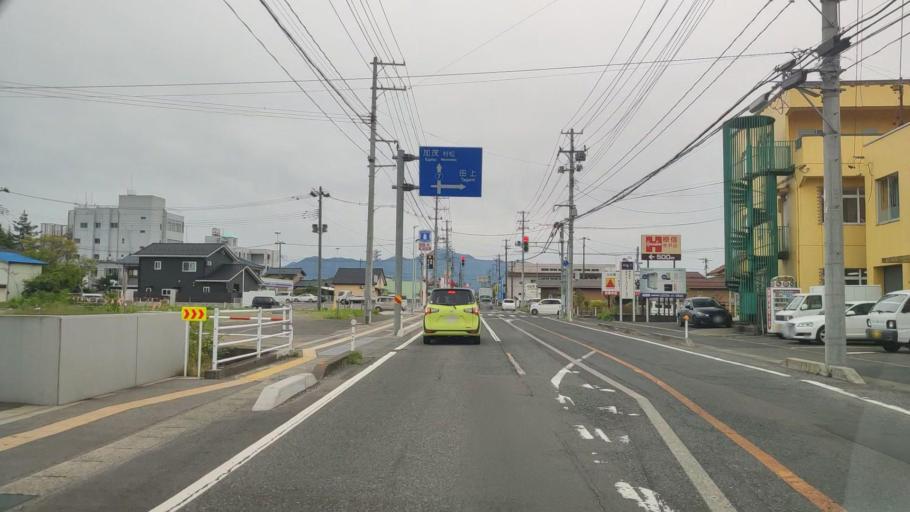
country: JP
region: Niigata
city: Gosen
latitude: 37.7299
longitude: 139.1771
